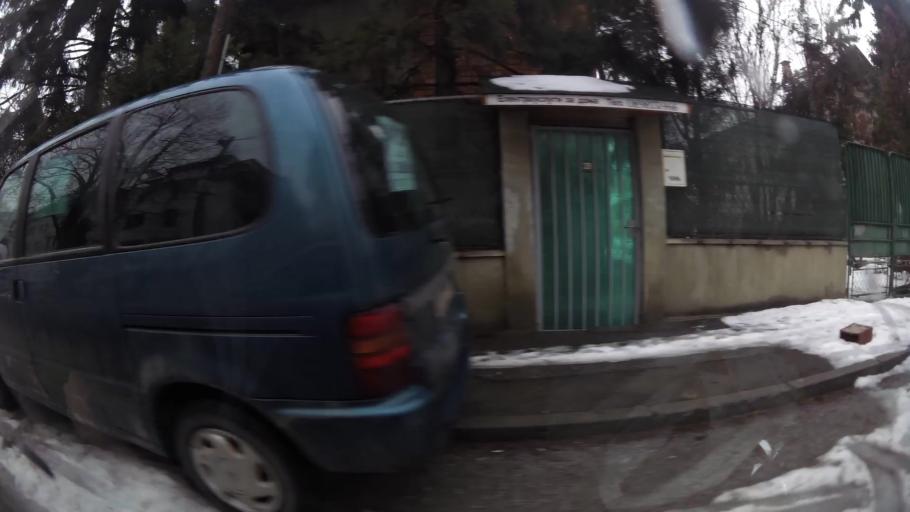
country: BG
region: Sofia-Capital
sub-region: Stolichna Obshtina
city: Sofia
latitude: 42.6625
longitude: 23.2704
